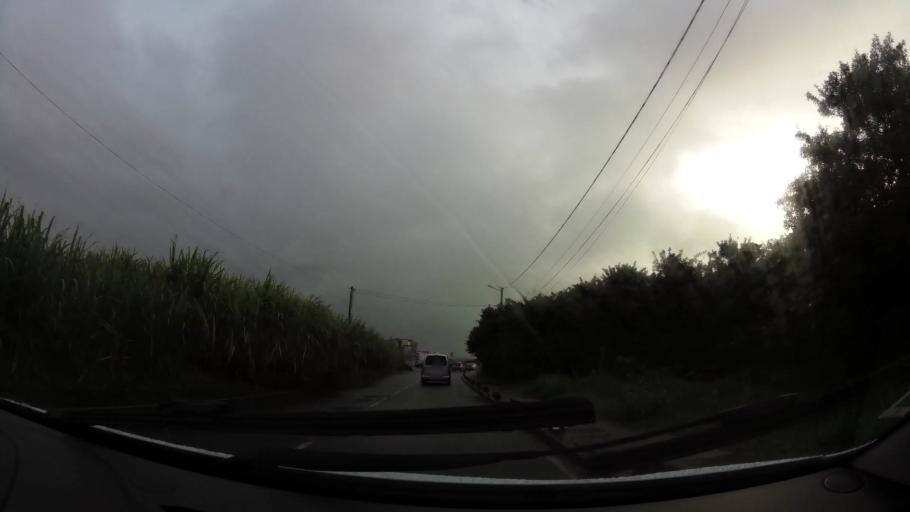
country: RE
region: Reunion
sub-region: Reunion
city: Saint-Andre
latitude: -20.9591
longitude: 55.6639
